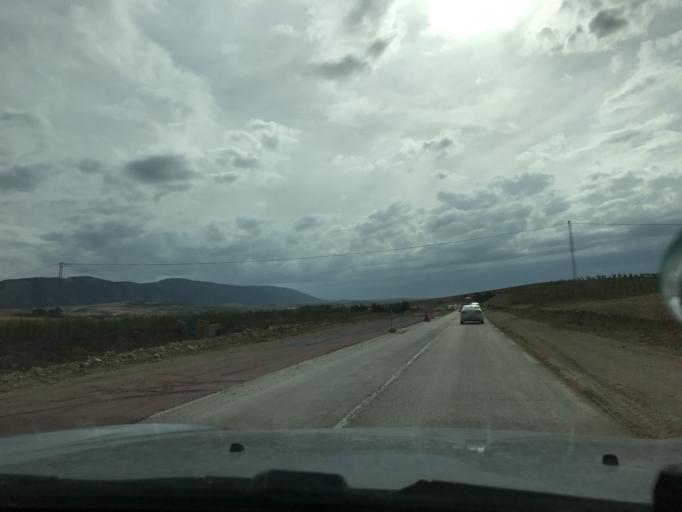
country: TN
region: Silyanah
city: Bu `Aradah
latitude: 36.1536
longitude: 9.6363
